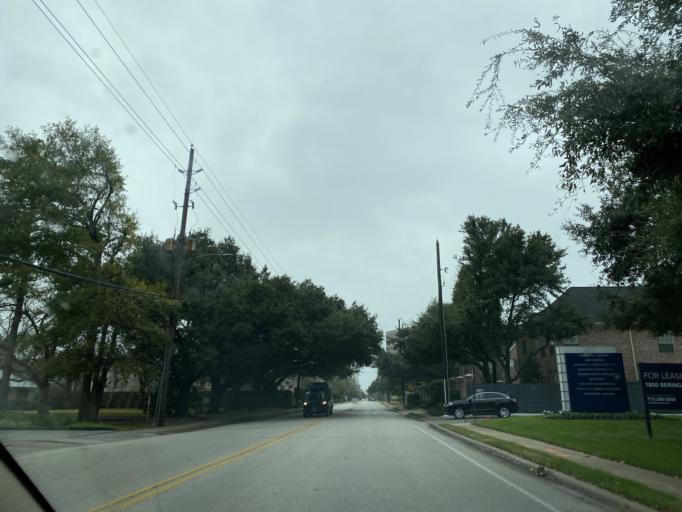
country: US
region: Texas
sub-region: Harris County
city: Hunters Creek Village
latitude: 29.7485
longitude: -95.4796
